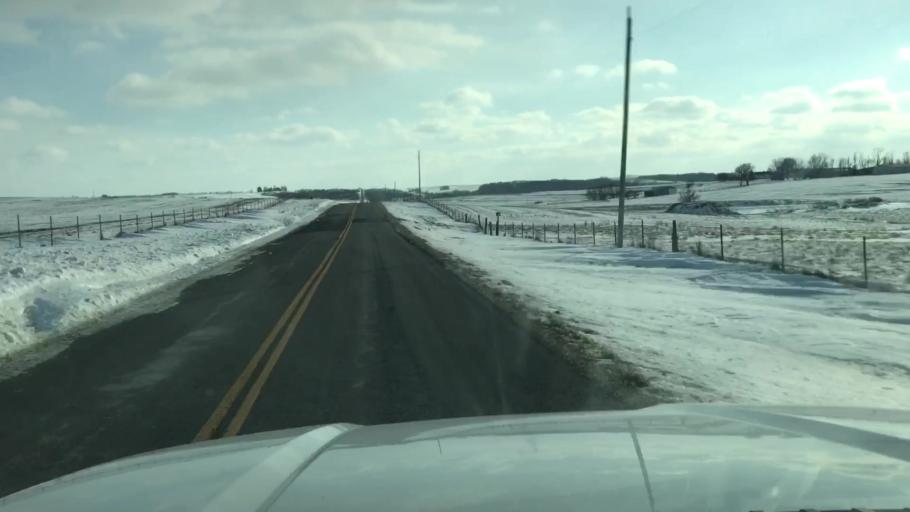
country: US
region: Missouri
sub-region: Nodaway County
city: Maryville
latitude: 40.1861
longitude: -95.0122
